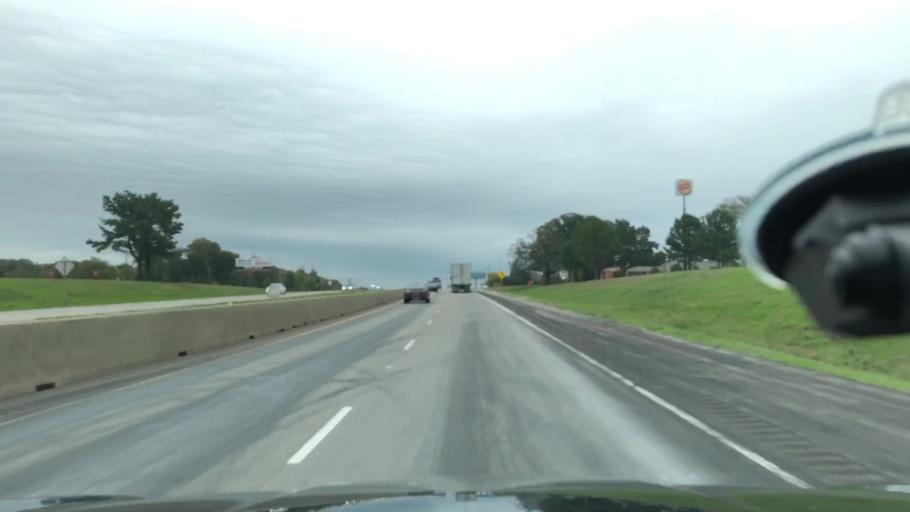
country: US
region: Texas
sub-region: Franklin County
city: Mount Vernon
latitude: 33.1618
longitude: -95.2348
